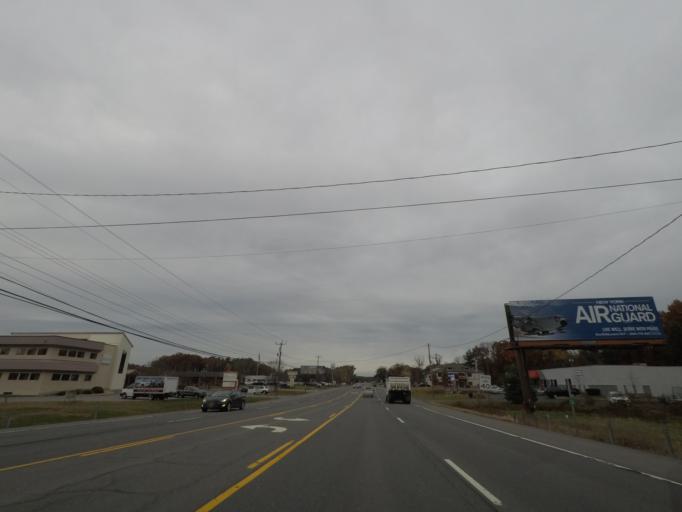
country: US
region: New York
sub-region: Saratoga County
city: Country Knolls
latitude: 42.8754
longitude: -73.7739
